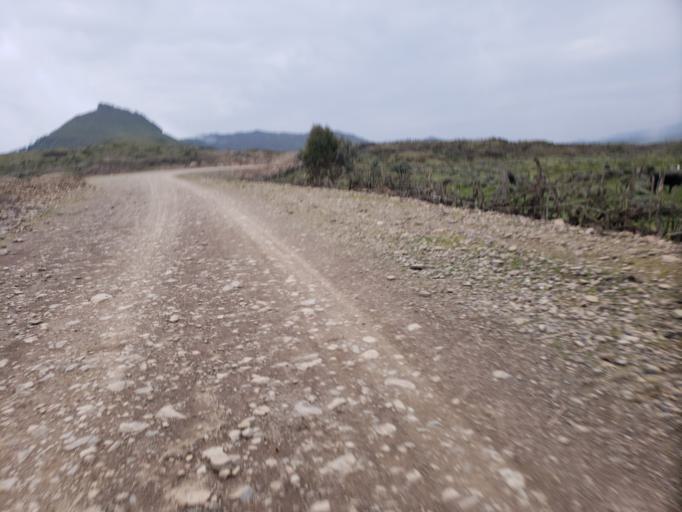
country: ET
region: Oromiya
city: Dodola
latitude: 6.7298
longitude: 39.4286
